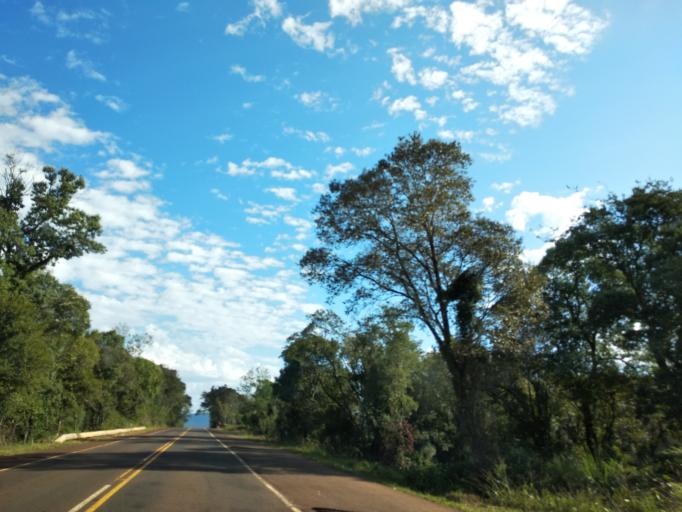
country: AR
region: Misiones
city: Aristobulo del Valle
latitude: -27.0964
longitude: -54.9558
